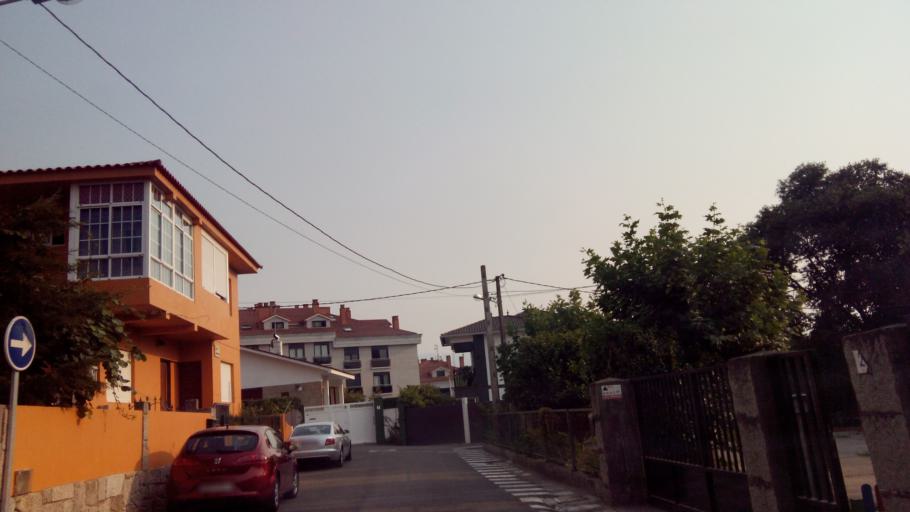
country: ES
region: Galicia
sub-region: Provincia de Pontevedra
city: Nigran
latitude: 42.1408
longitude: -8.8073
